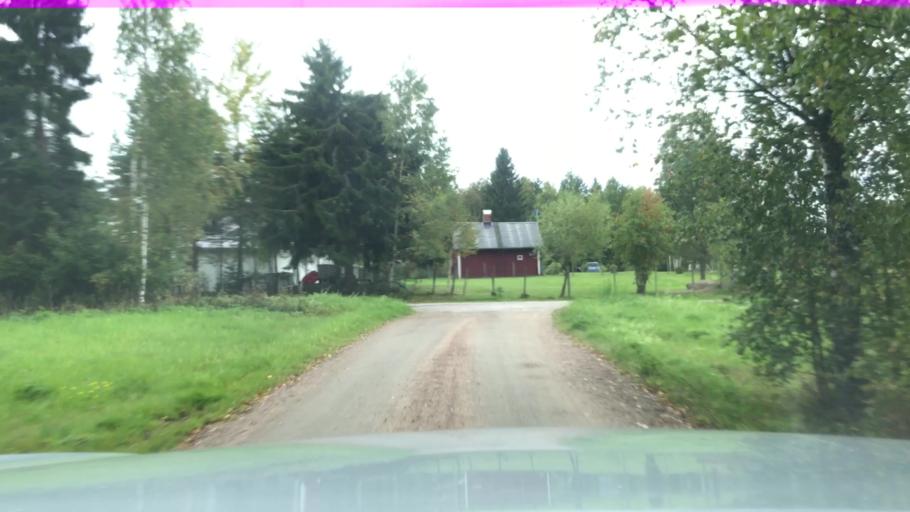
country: SE
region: Vaermland
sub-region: Munkfors Kommun
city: Munkfors
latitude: 59.8401
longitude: 13.5009
